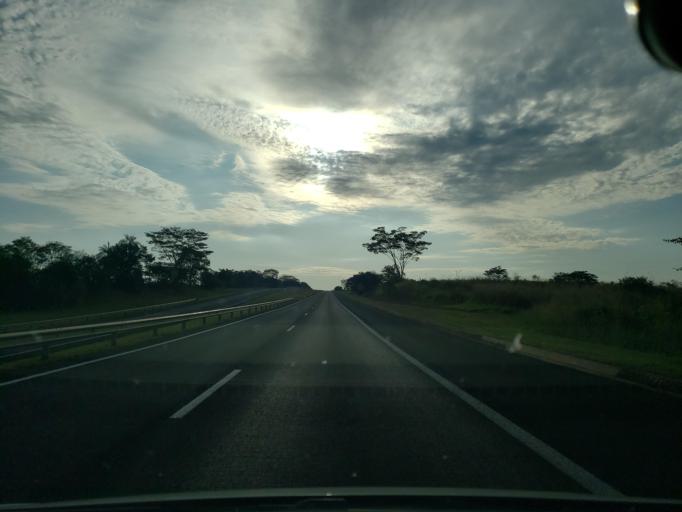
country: BR
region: Sao Paulo
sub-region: Mirandopolis
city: Mirandopolis
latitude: -21.0989
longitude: -51.0426
